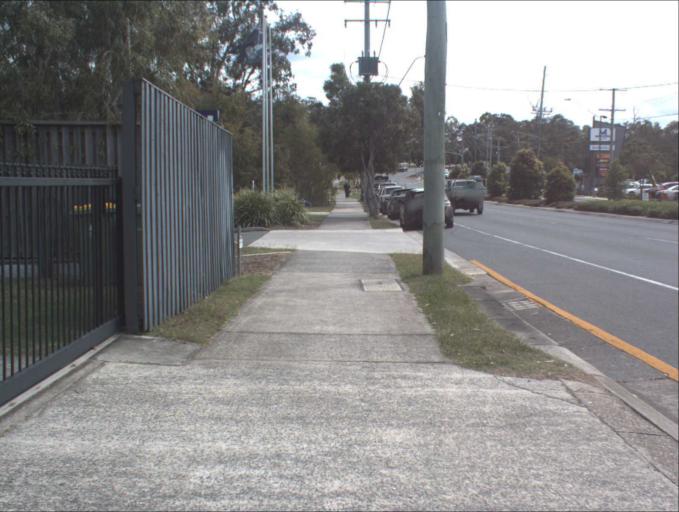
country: AU
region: Queensland
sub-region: Logan
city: Logan Reserve
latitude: -27.6785
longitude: 153.0822
